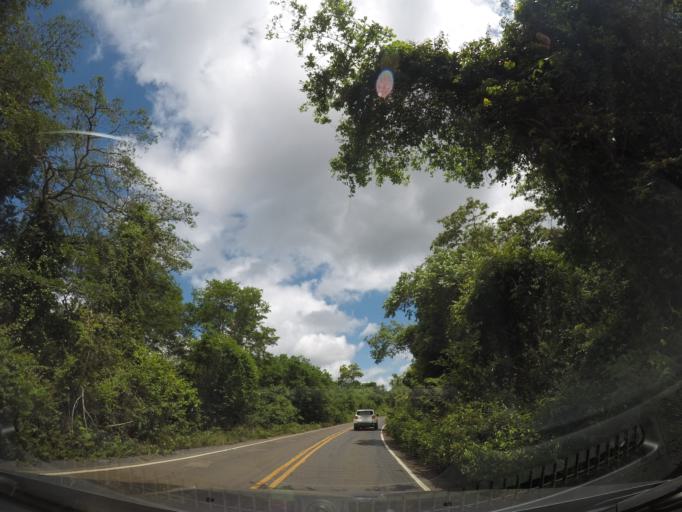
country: BR
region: Bahia
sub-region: Andarai
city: Vera Cruz
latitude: -12.4991
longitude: -41.3637
